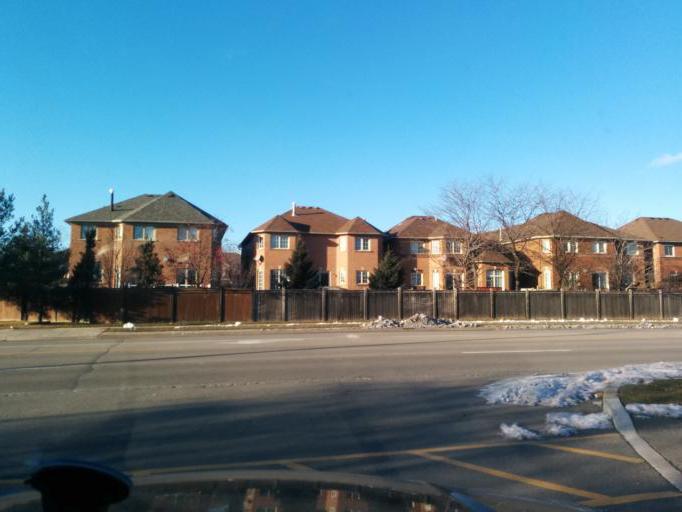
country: CA
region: Ontario
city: Mississauga
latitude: 43.5791
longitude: -79.6604
